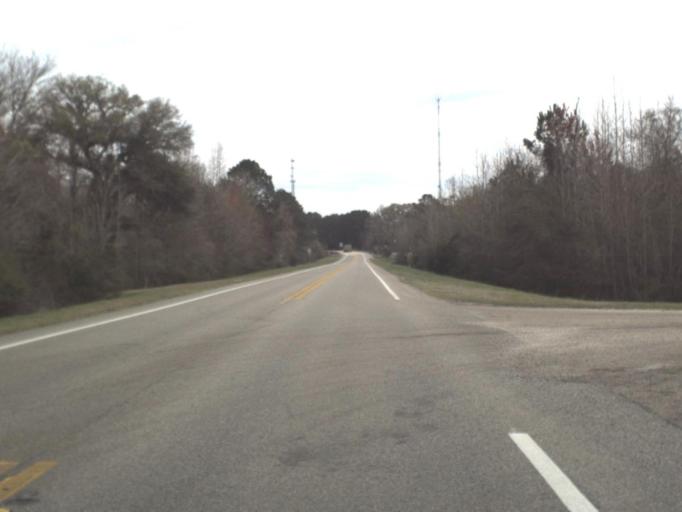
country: US
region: Florida
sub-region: Gadsden County
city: Quincy
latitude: 30.3865
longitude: -84.6576
